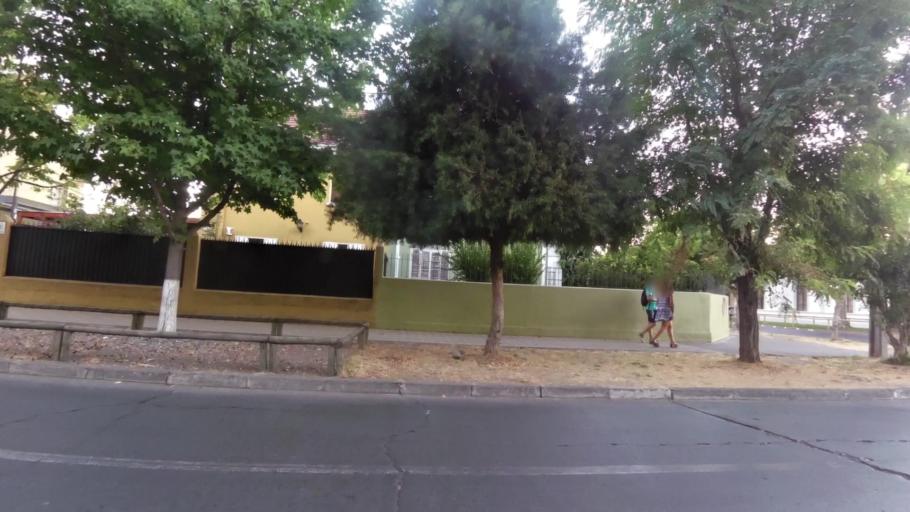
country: CL
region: Maule
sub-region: Provincia de Curico
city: Curico
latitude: -34.9894
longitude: -71.2393
